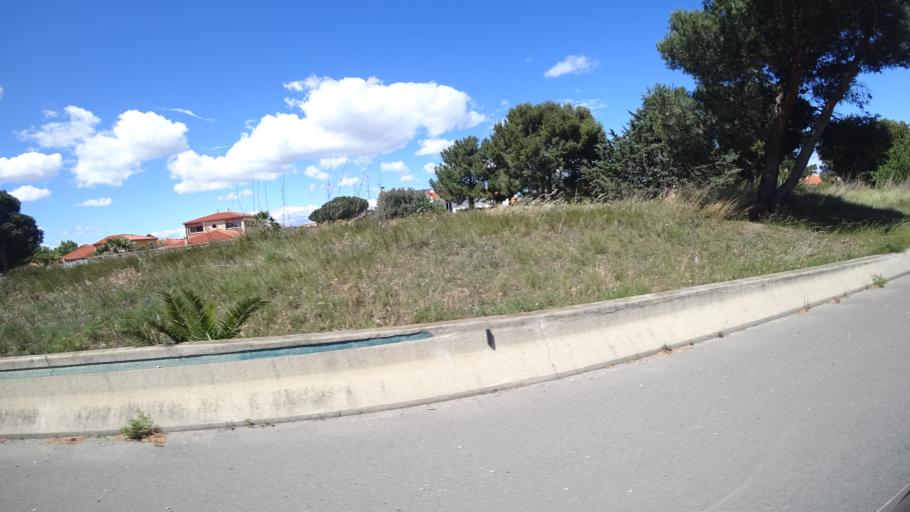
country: FR
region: Languedoc-Roussillon
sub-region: Departement des Pyrenees-Orientales
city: Canet-en-Roussillon
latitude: 42.7026
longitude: 3.0117
